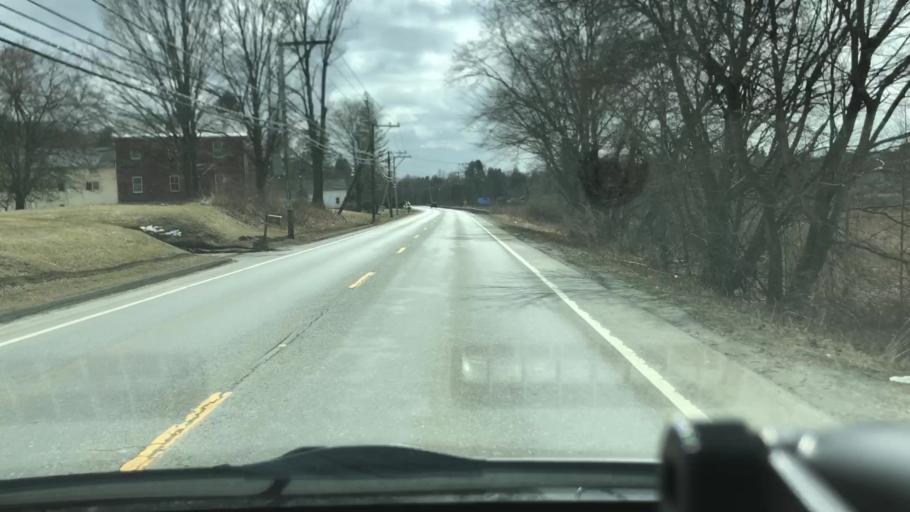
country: US
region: Massachusetts
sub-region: Franklin County
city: Greenfield
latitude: 42.5556
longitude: -72.5984
